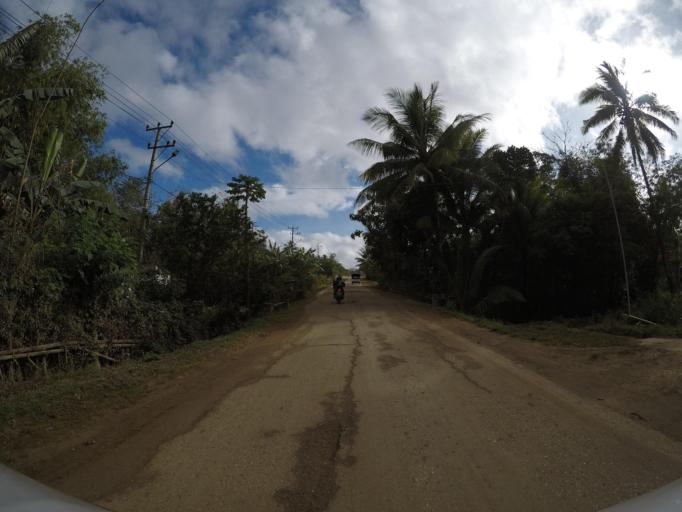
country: TL
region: Lautem
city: Lospalos
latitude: -8.4987
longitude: 126.9910
